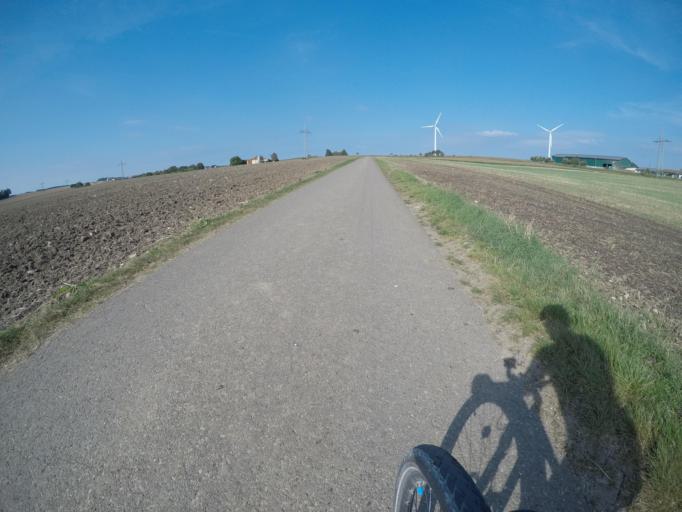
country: DE
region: Baden-Wuerttemberg
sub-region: Regierungsbezirk Stuttgart
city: Bohmenkirch
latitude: 48.6425
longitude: 9.9335
